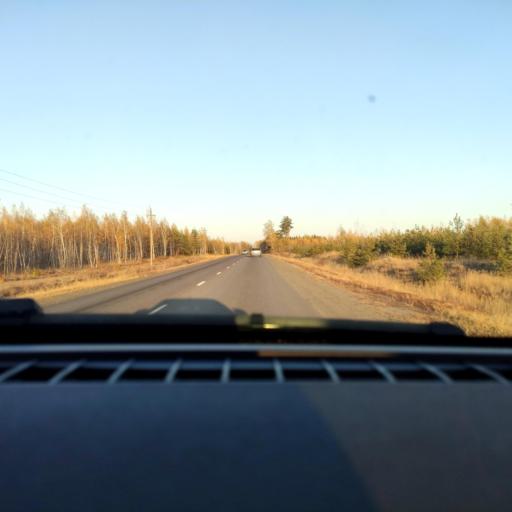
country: RU
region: Voronezj
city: Maslovka
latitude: 51.5788
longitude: 39.2702
